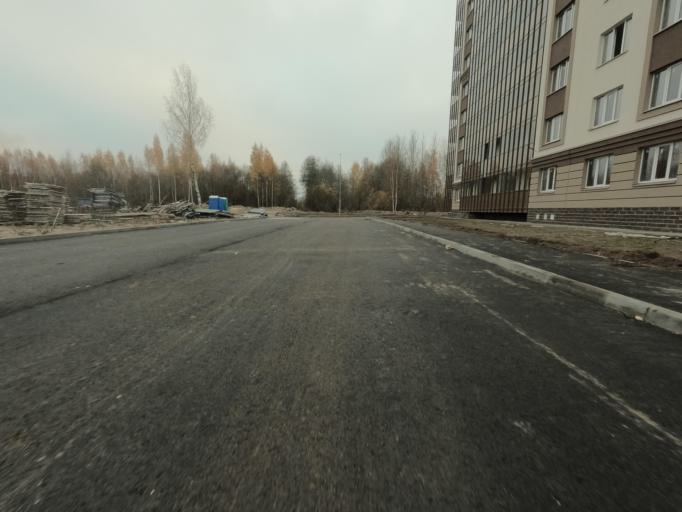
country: RU
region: Leningrad
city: Kirovsk
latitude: 59.8789
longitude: 31.0094
